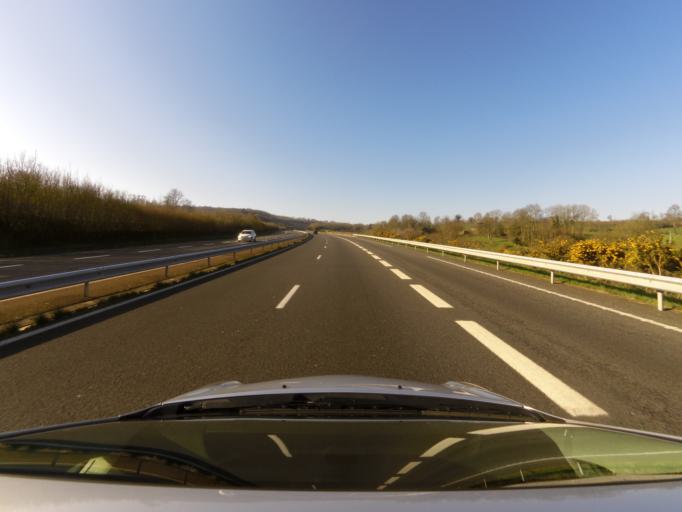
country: FR
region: Lower Normandy
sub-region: Departement de la Manche
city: Tessy-sur-Vire
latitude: 48.9330
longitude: -1.0727
